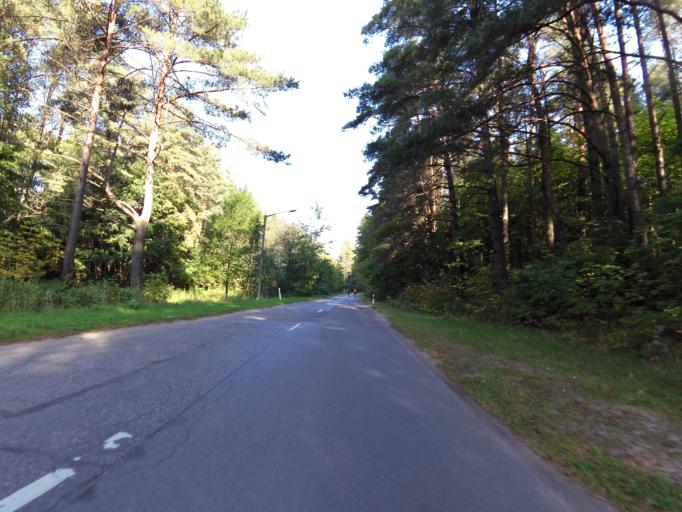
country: LT
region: Vilnius County
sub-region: Vilnius
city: Vilnius
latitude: 54.7387
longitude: 25.2939
